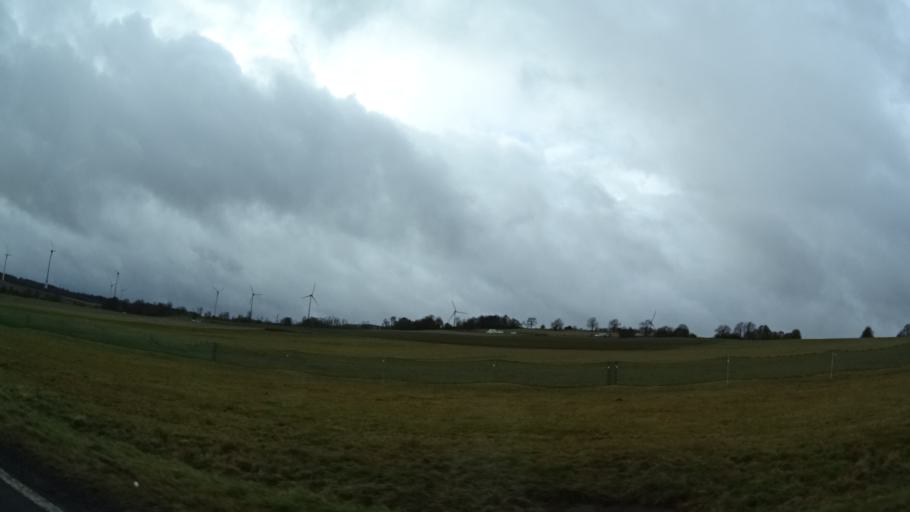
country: DE
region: Hesse
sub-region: Regierungsbezirk Giessen
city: Lautertal
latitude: 50.6199
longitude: 9.2709
